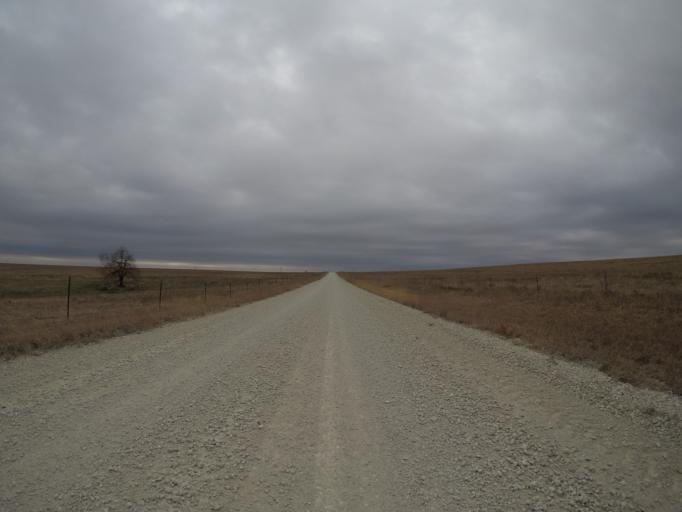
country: US
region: Kansas
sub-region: Wabaunsee County
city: Alma
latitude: 38.7631
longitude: -96.1497
